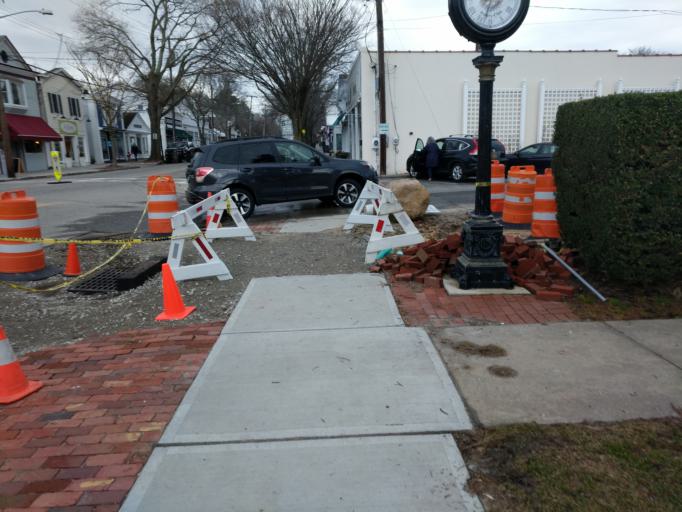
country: US
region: New York
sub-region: Suffolk County
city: Southampton
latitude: 40.8831
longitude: -72.3924
